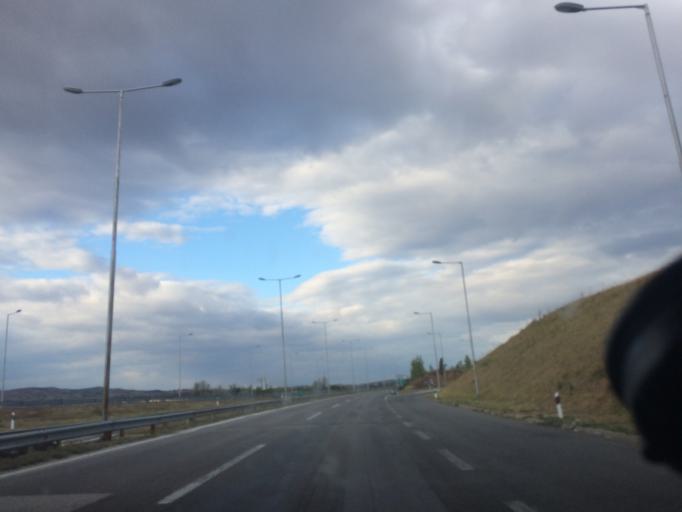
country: MK
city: Miladinovci
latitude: 41.9589
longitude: 21.6321
